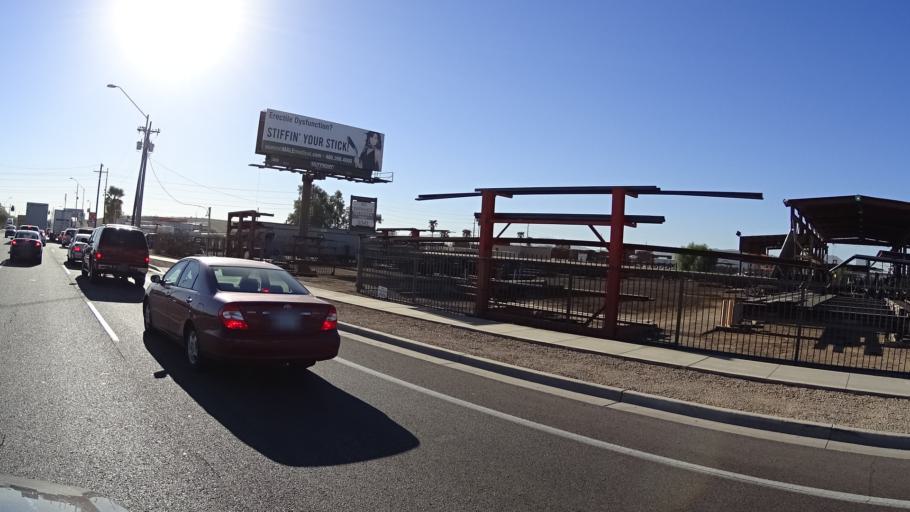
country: US
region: Arizona
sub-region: Maricopa County
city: Phoenix
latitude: 33.4225
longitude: -112.1363
